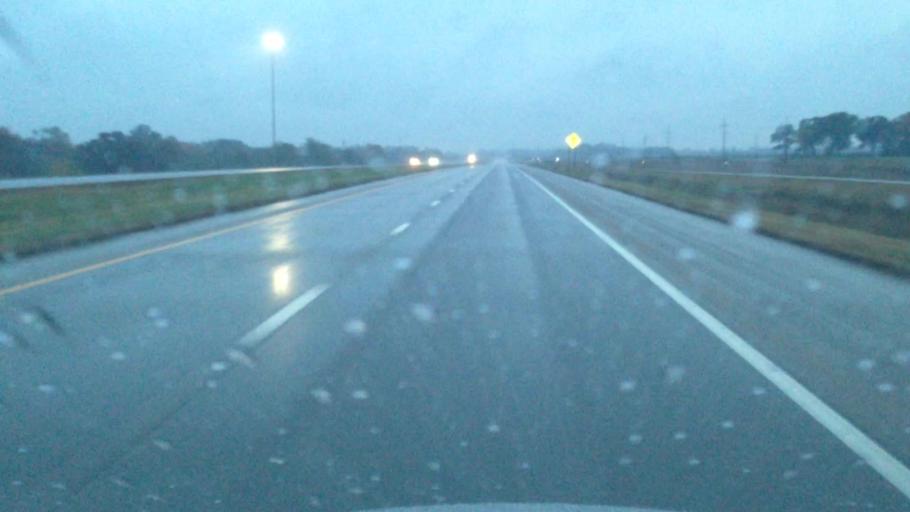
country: US
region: Kansas
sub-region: Franklin County
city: Ottawa
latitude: 38.7081
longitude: -95.2685
